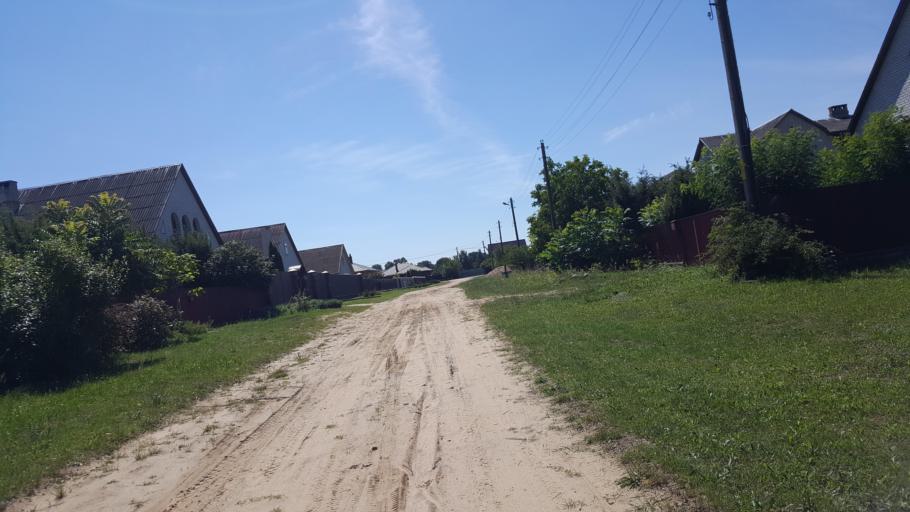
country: BY
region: Brest
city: Charnawchytsy
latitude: 52.2125
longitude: 23.7357
